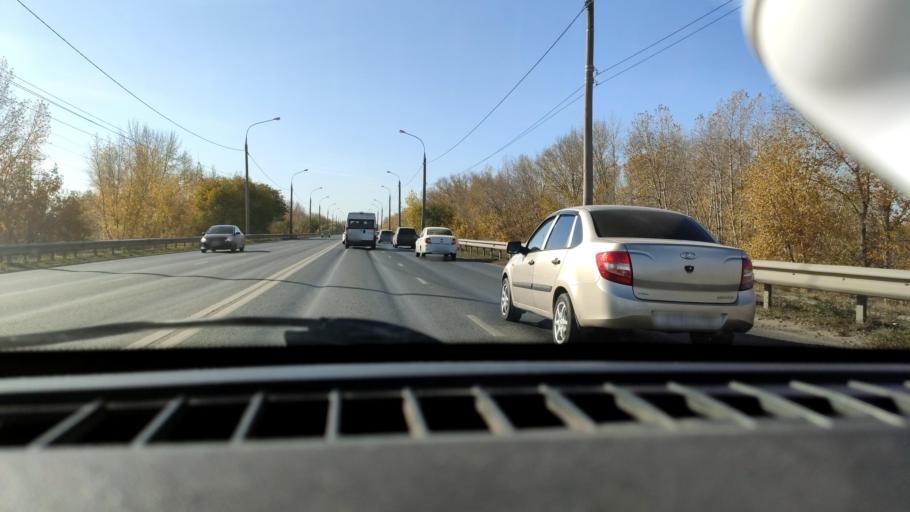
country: RU
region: Samara
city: Samara
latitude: 53.1541
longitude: 50.1896
